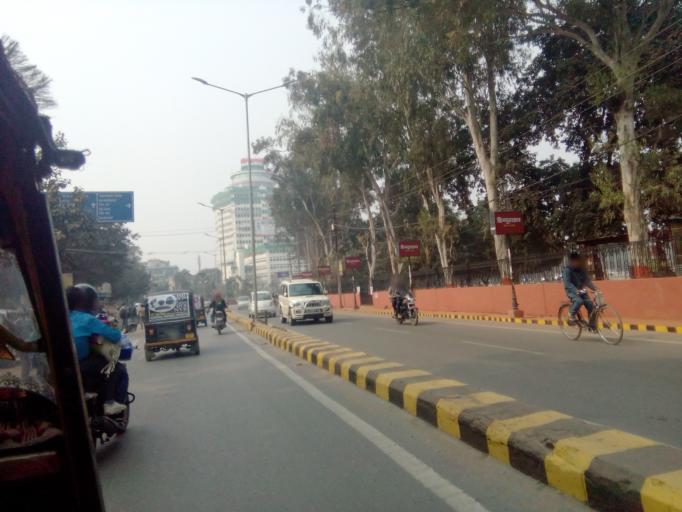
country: IN
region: Bihar
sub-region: Patna
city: Patna
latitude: 25.6159
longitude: 85.1434
